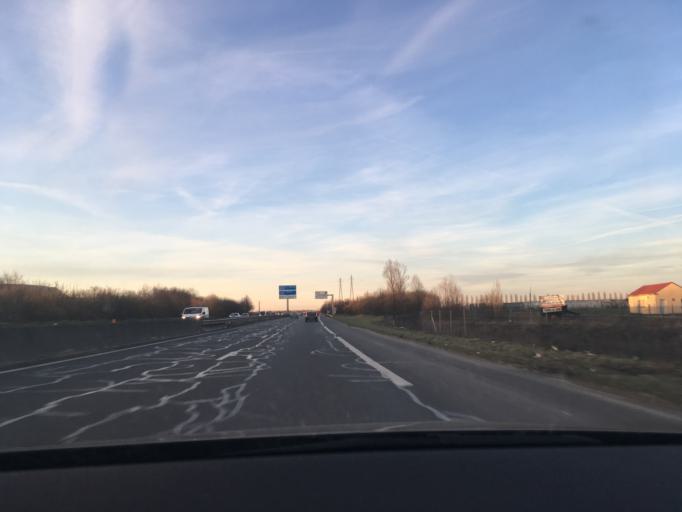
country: FR
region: Ile-de-France
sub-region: Departement de Seine-et-Marne
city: Vert-Saint-Denis
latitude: 48.5689
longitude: 2.6419
